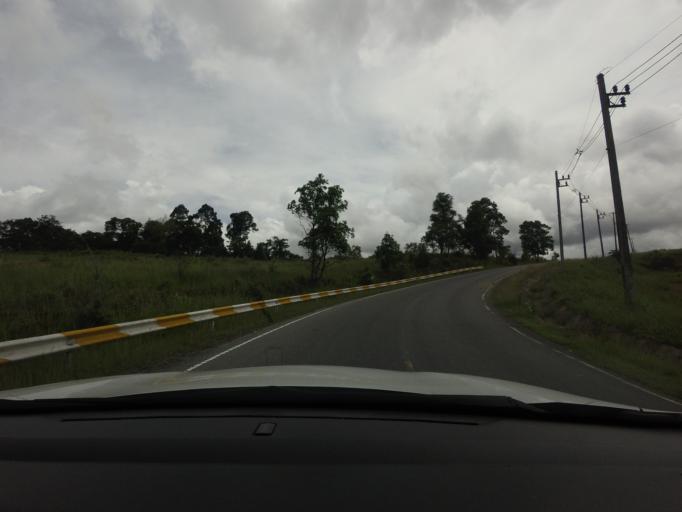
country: TH
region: Nakhon Nayok
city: Nakhon Nayok
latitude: 14.4279
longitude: 101.3686
